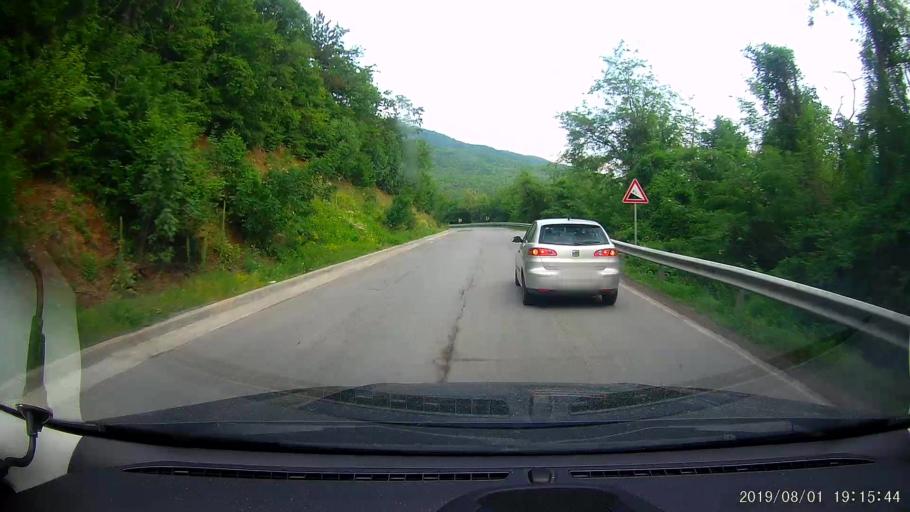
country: BG
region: Shumen
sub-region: Obshtina Smyadovo
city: Smyadovo
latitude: 42.9301
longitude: 26.9442
